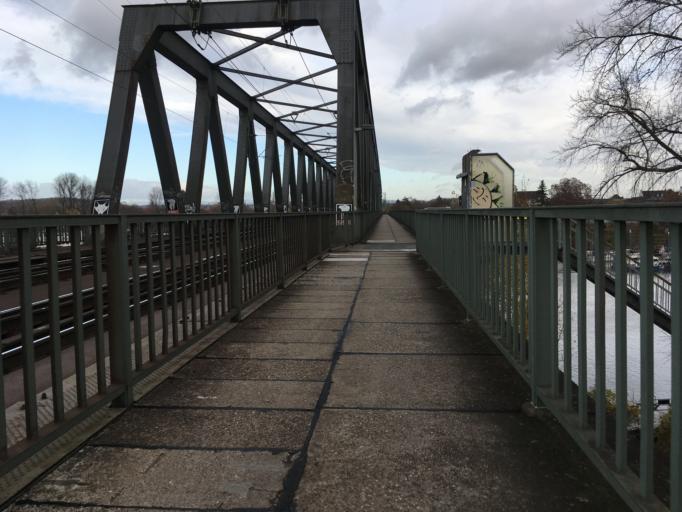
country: DE
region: Rheinland-Pfalz
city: Mainz
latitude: 50.0245
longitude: 8.2578
